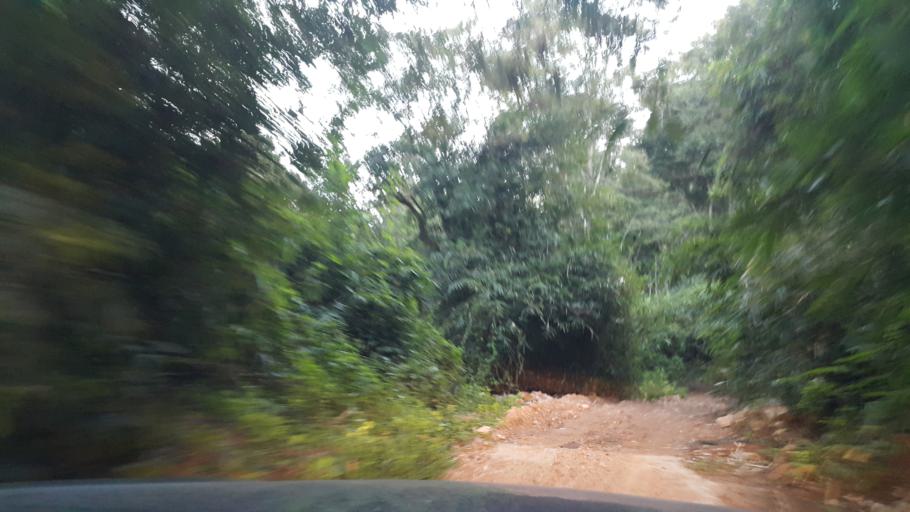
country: TH
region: Lamphun
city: Ban Thi
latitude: 18.6800
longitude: 99.2060
